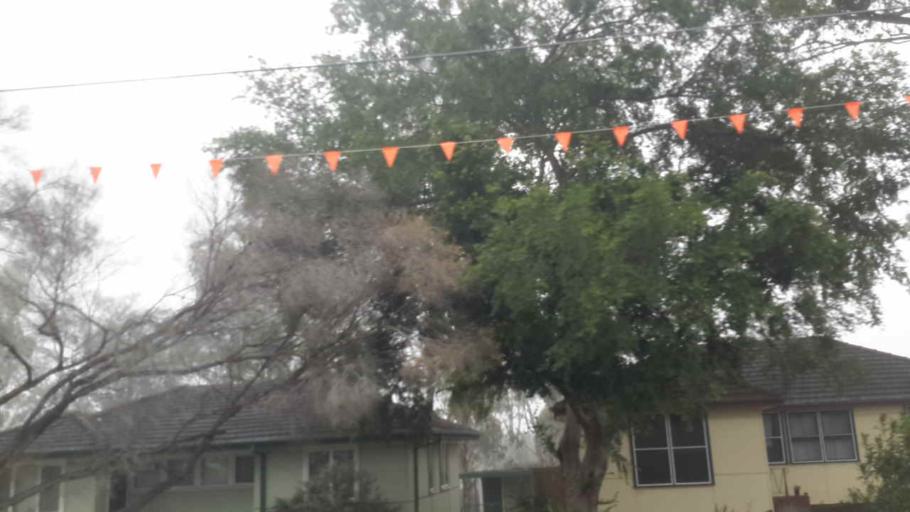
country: AU
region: New South Wales
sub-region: Penrith Municipality
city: Kingswood Park
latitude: -33.7654
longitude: 150.7096
